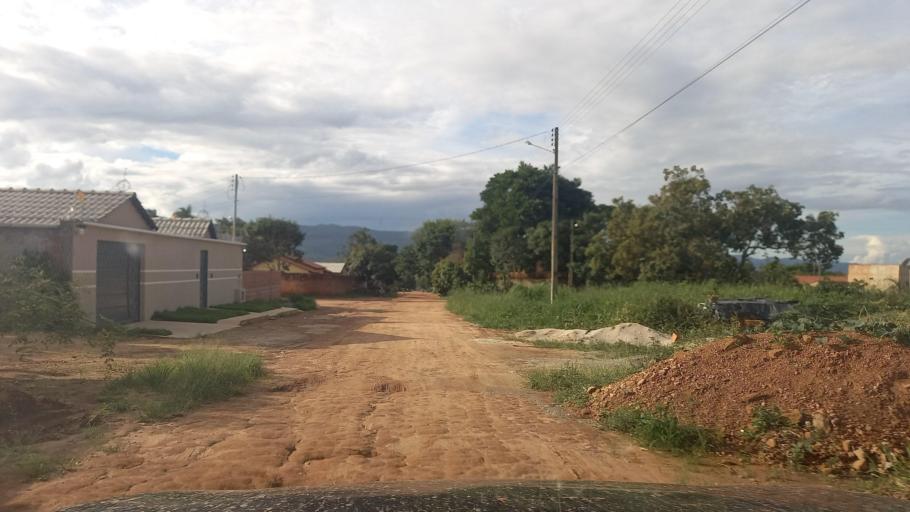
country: BR
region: Goias
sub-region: Cavalcante
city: Cavalcante
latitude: -13.7991
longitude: -47.4411
